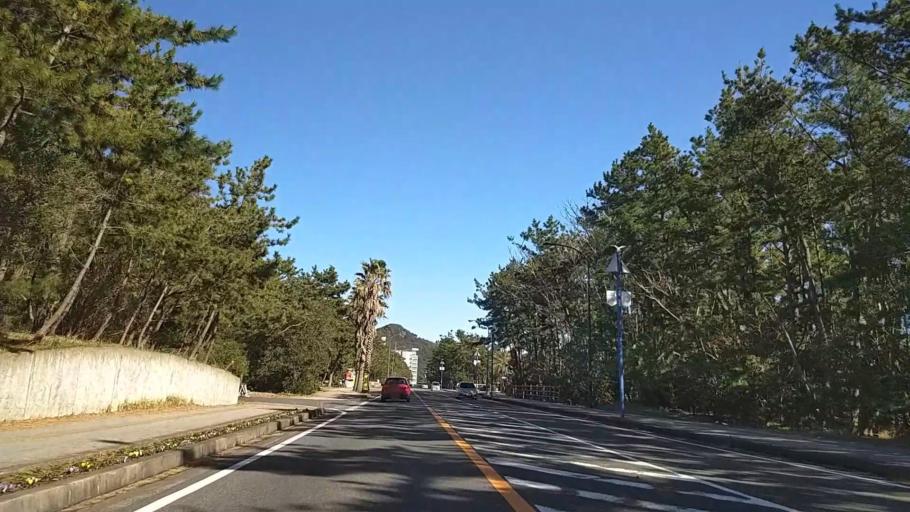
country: JP
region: Chiba
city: Kawaguchi
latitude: 35.1162
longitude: 140.1196
